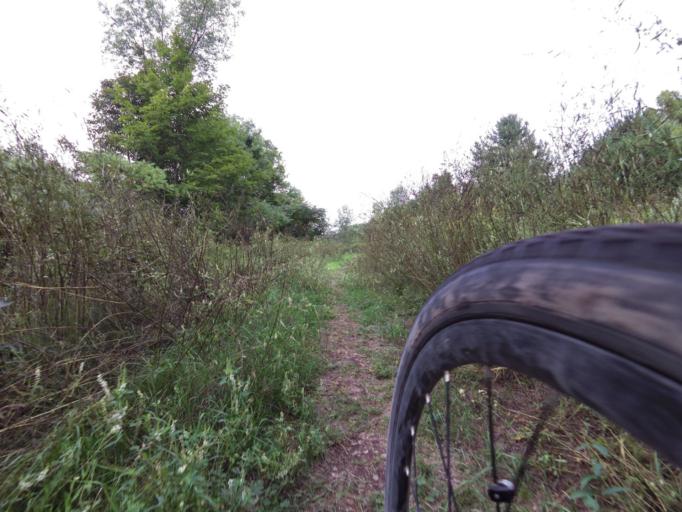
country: CA
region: Ontario
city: Gananoque
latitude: 44.5785
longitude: -76.3257
